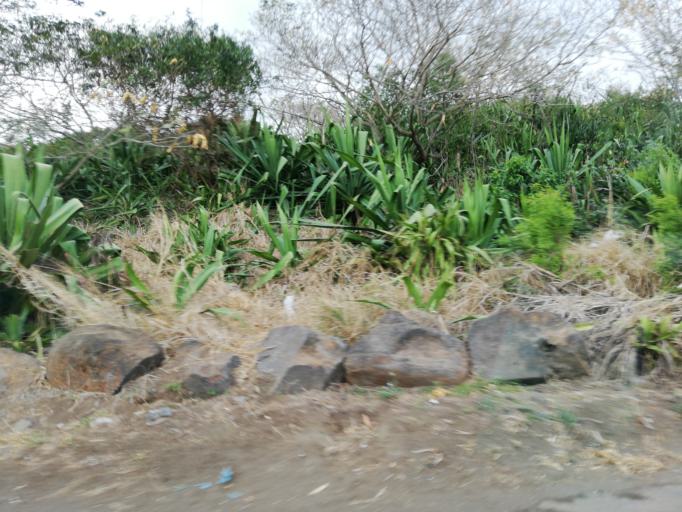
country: MU
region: Black River
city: Petite Riviere
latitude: -20.2093
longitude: 57.4655
